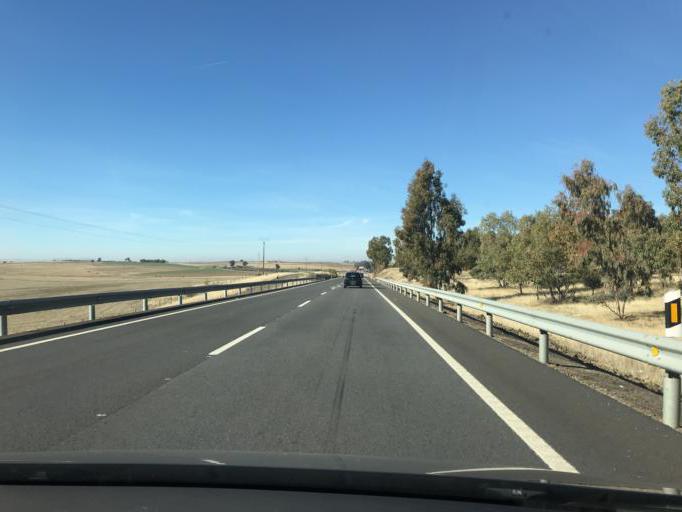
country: ES
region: Extremadura
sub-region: Provincia de Badajoz
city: Granja de Torrehermosa
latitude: 38.3006
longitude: -5.5998
